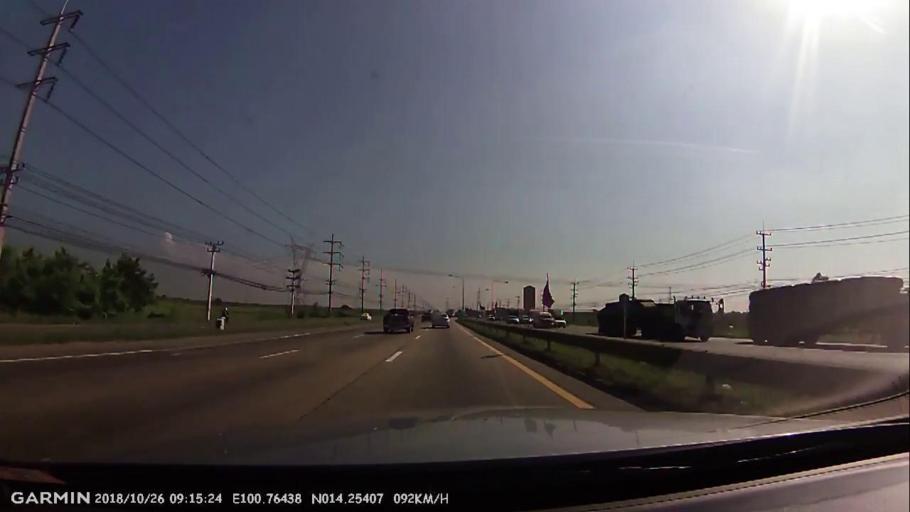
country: TH
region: Phra Nakhon Si Ayutthaya
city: Wang Noi
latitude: 14.2543
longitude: 100.7633
